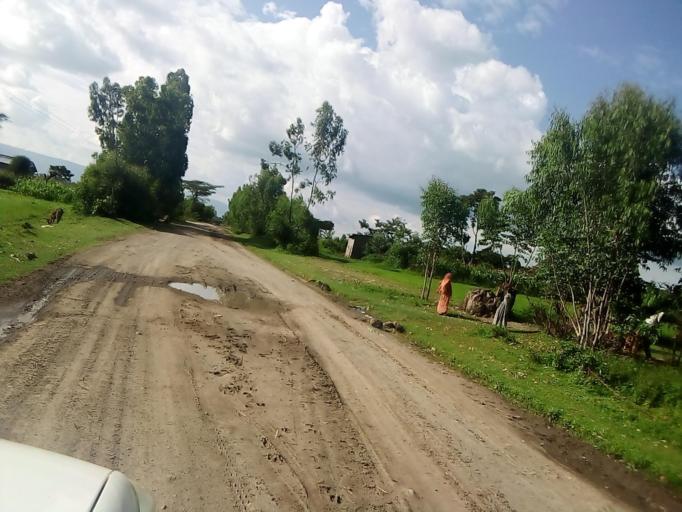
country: ET
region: Southern Nations, Nationalities, and People's Region
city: K'olito
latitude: 7.6548
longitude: 38.0490
